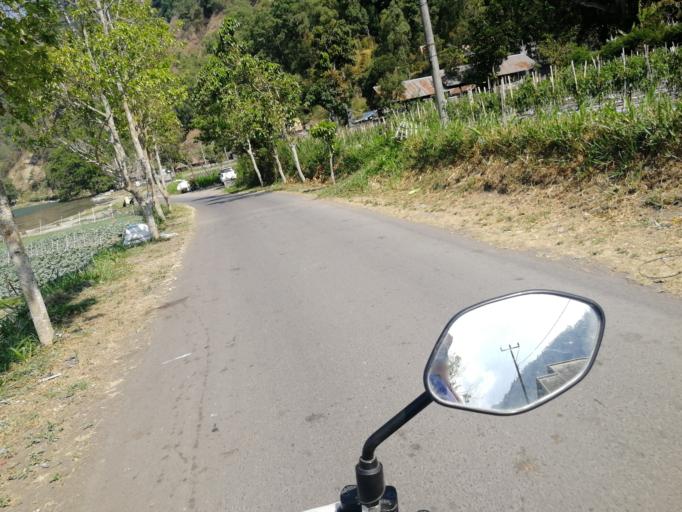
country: ID
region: Bali
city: Banjar Buahan
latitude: -8.2870
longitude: 115.3927
